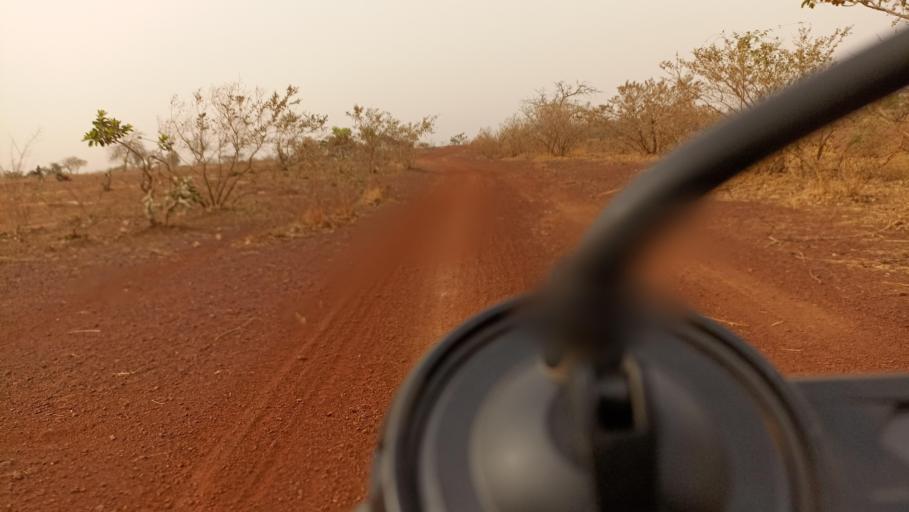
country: BF
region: Nord
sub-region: Province du Zondoma
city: Gourcy
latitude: 13.1527
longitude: -2.5954
